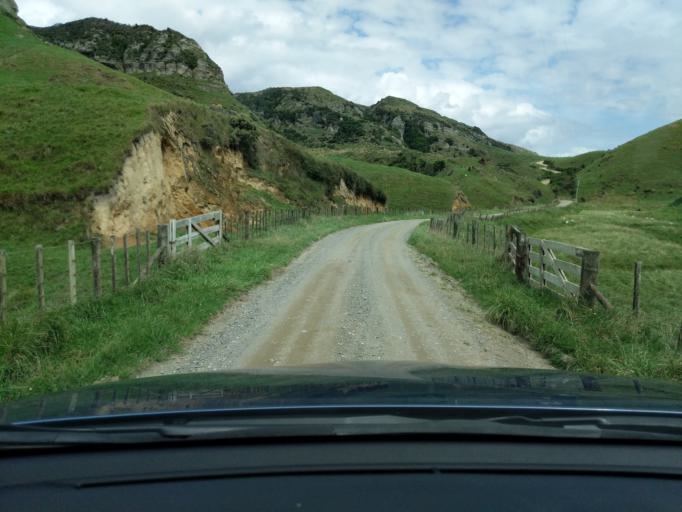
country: NZ
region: Tasman
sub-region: Tasman District
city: Takaka
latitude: -40.6552
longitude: 172.4188
